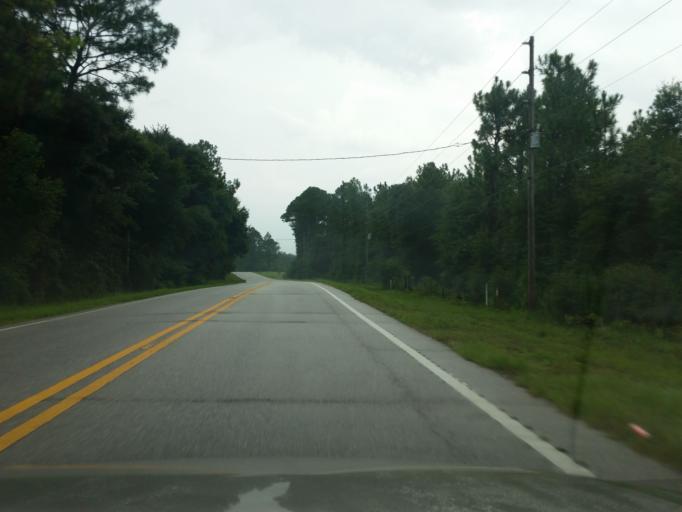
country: US
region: Alabama
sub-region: Baldwin County
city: Elberta
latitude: 30.5206
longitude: -87.4869
